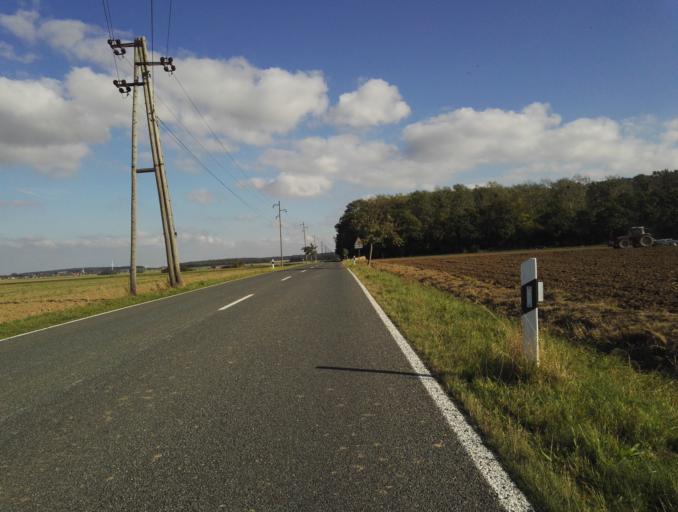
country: DE
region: Lower Saxony
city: Schellerten
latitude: 52.1495
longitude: 10.1053
